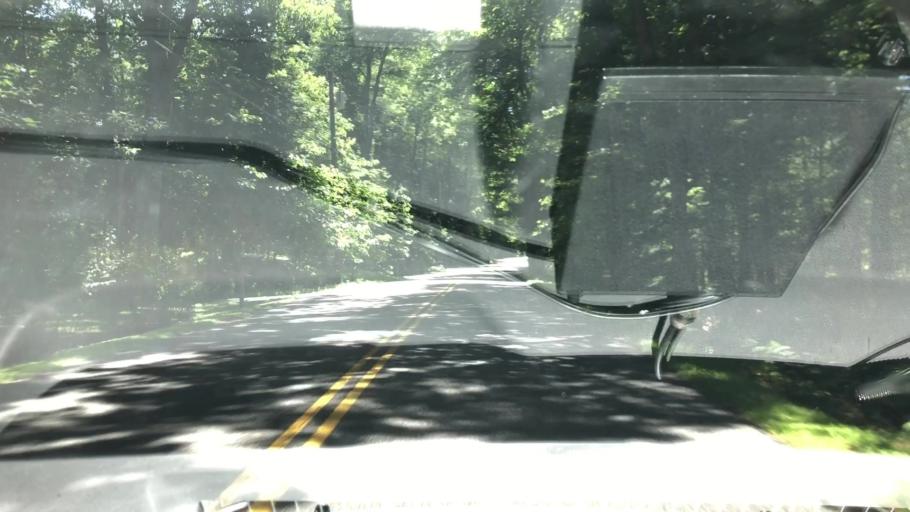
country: US
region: New Hampshire
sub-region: Hillsborough County
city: Milford
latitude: 42.8626
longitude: -71.5980
